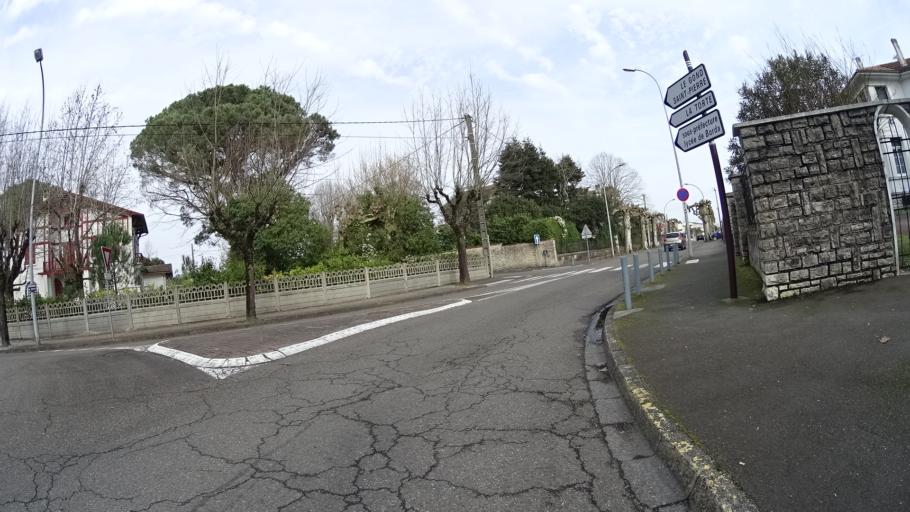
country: FR
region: Aquitaine
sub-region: Departement des Landes
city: Dax
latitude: 43.7037
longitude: -1.0566
